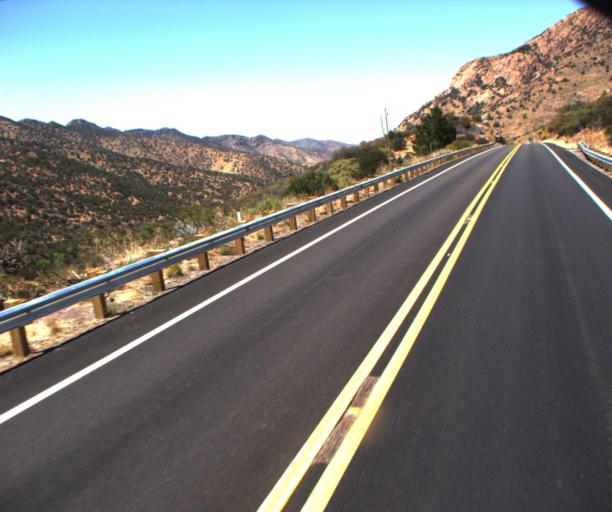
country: US
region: Arizona
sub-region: Cochise County
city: Bisbee
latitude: 31.4611
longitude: -109.9462
